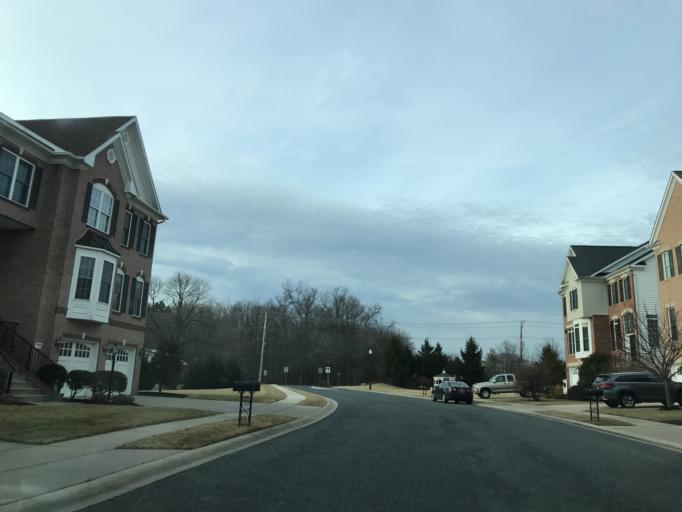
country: US
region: Maryland
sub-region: Harford County
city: Pleasant Hills
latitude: 39.4989
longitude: -76.3944
